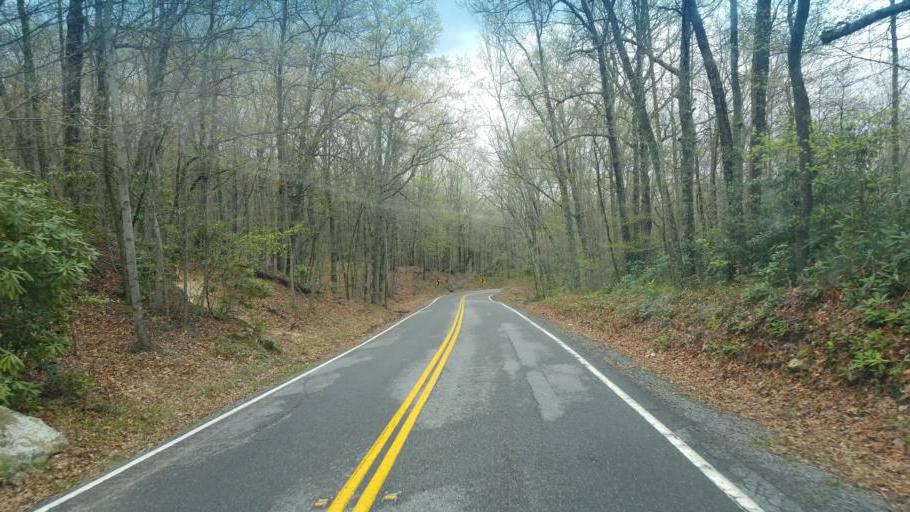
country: US
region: Virginia
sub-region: Tazewell County
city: Tazewell
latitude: 36.9940
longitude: -81.5316
